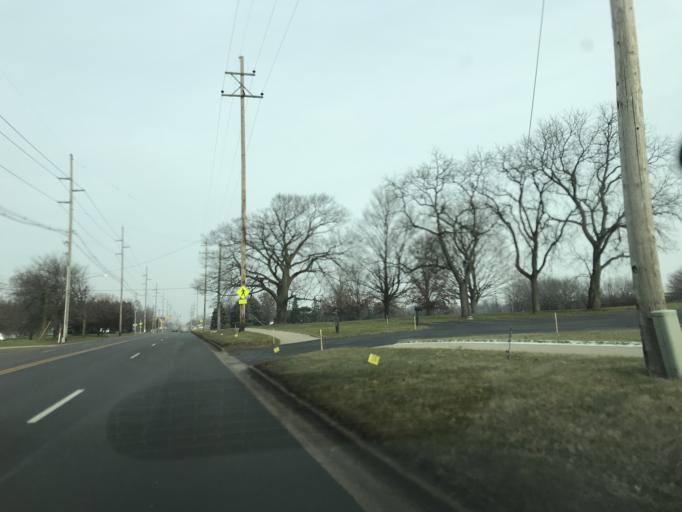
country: US
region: Michigan
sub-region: Ottawa County
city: Holland
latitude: 42.7700
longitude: -86.0773
